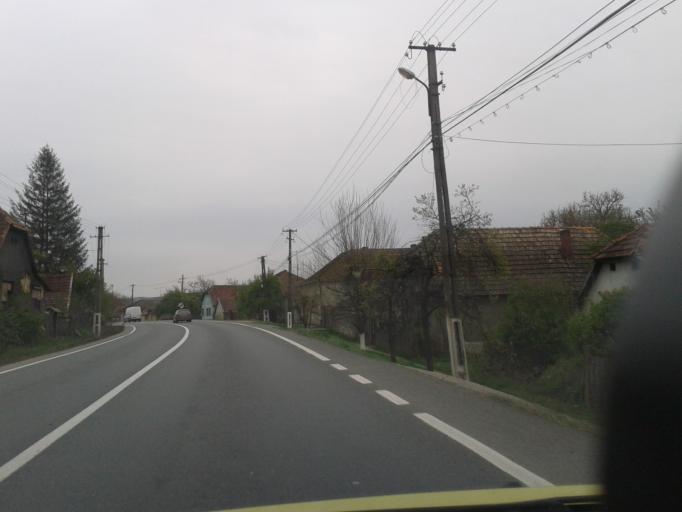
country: RO
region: Arad
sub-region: Comuna Barzava
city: Barzava
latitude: 46.1078
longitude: 21.9827
